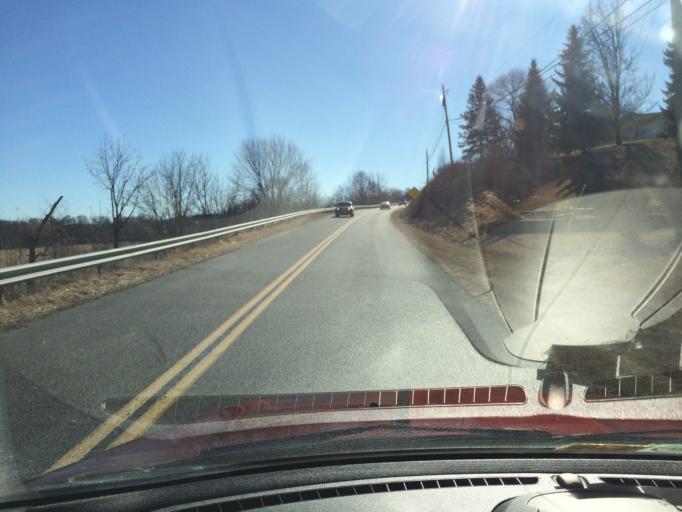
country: US
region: Virginia
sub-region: Rockingham County
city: Bridgewater
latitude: 38.3749
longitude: -78.9795
